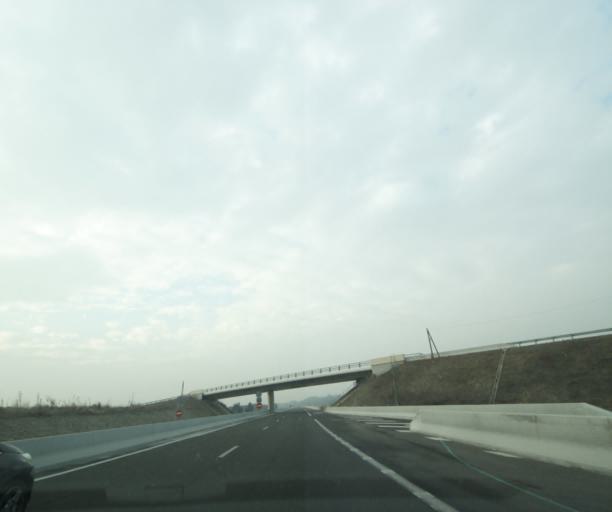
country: FR
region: Rhone-Alpes
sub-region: Departement du Rhone
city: Les Cheres
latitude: 45.9061
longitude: 4.7369
